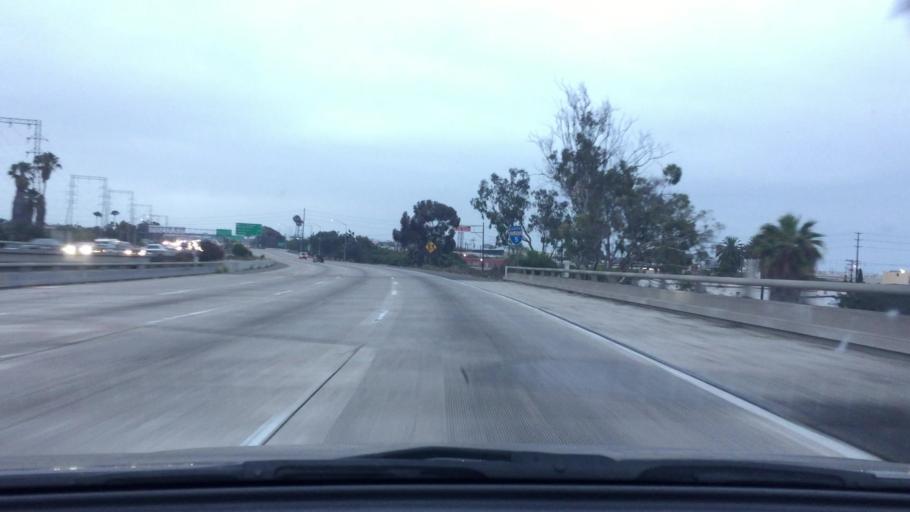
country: US
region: California
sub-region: San Diego County
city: National City
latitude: 32.6691
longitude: -117.1116
